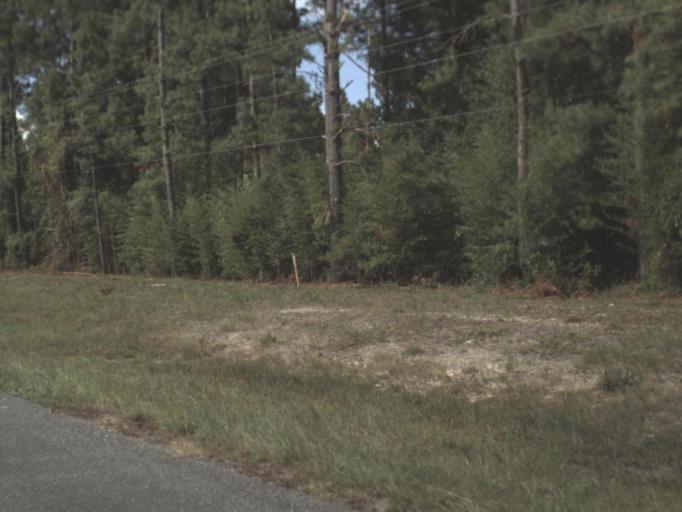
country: US
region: Florida
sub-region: Taylor County
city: Perry
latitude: 30.2642
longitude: -83.6261
